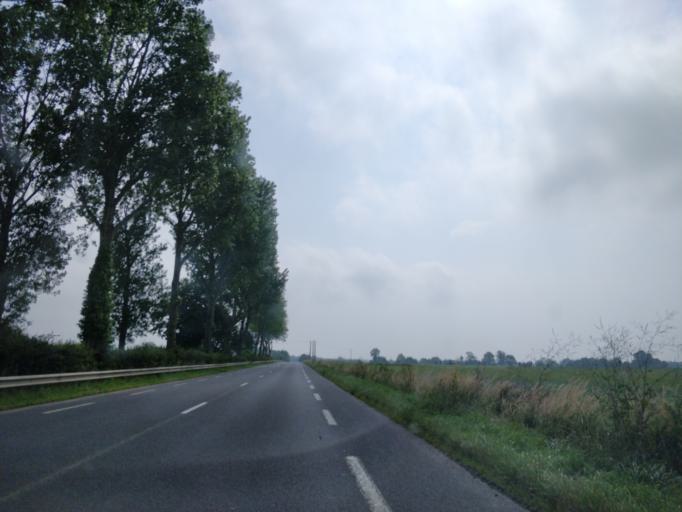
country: FR
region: Lower Normandy
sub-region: Departement du Calvados
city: Demouville
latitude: 49.1741
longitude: -0.2477
